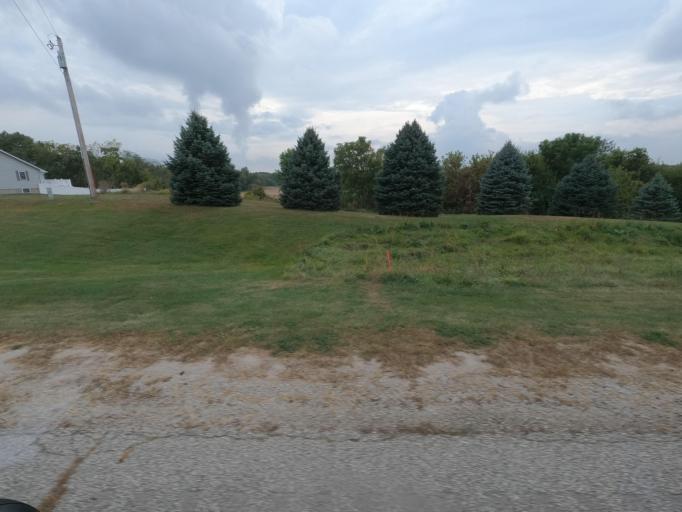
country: US
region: Iowa
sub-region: Wapello County
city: Eddyville
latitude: 41.1197
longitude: -92.5533
